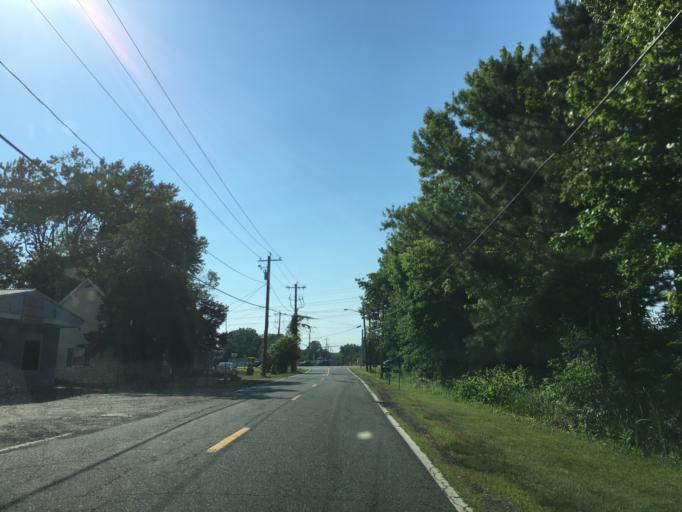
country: US
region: Maryland
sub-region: Queen Anne's County
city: Grasonville
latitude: 38.9867
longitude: -76.1512
